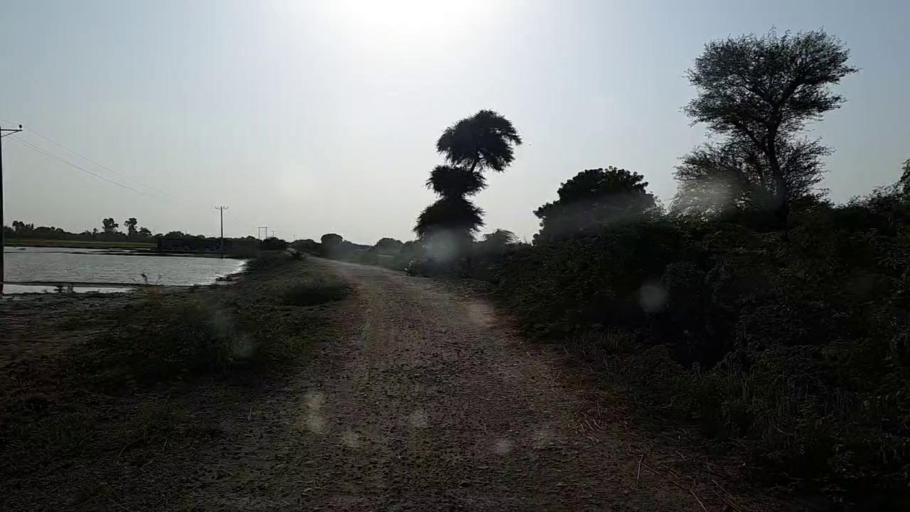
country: PK
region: Sindh
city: Bulri
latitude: 24.7670
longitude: 68.4253
